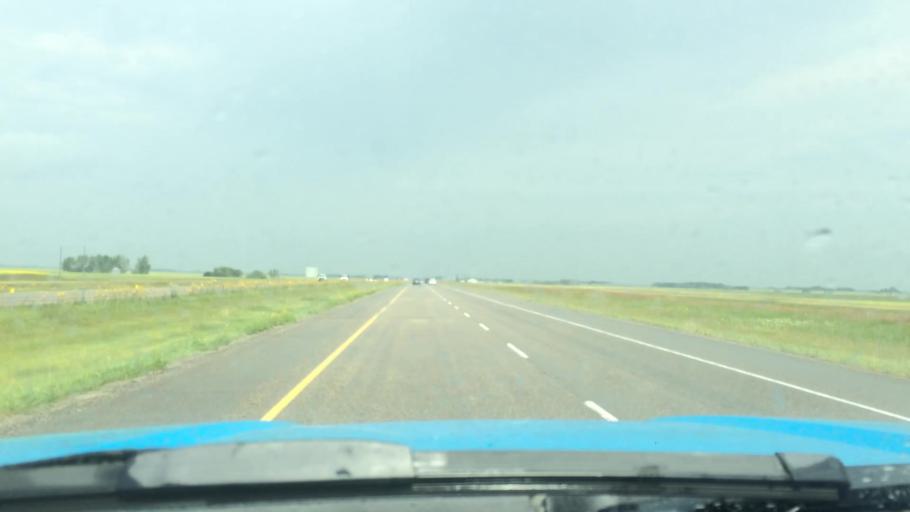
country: CA
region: Alberta
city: Didsbury
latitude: 51.6839
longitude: -114.0253
